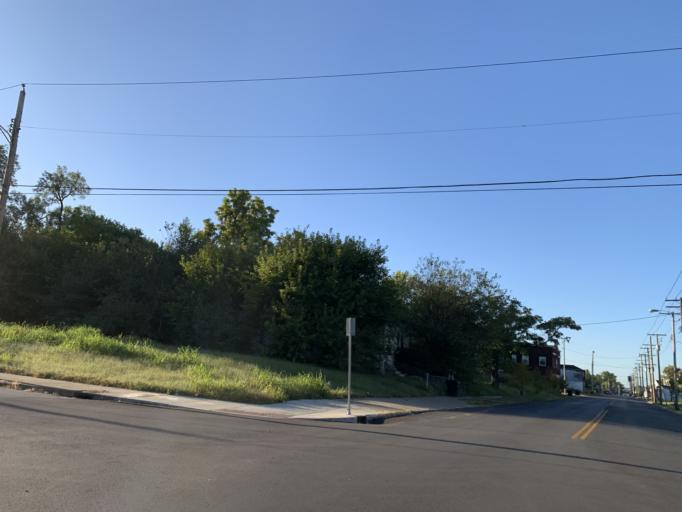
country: US
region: Kentucky
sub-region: Jefferson County
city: Louisville
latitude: 38.2421
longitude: -85.7849
